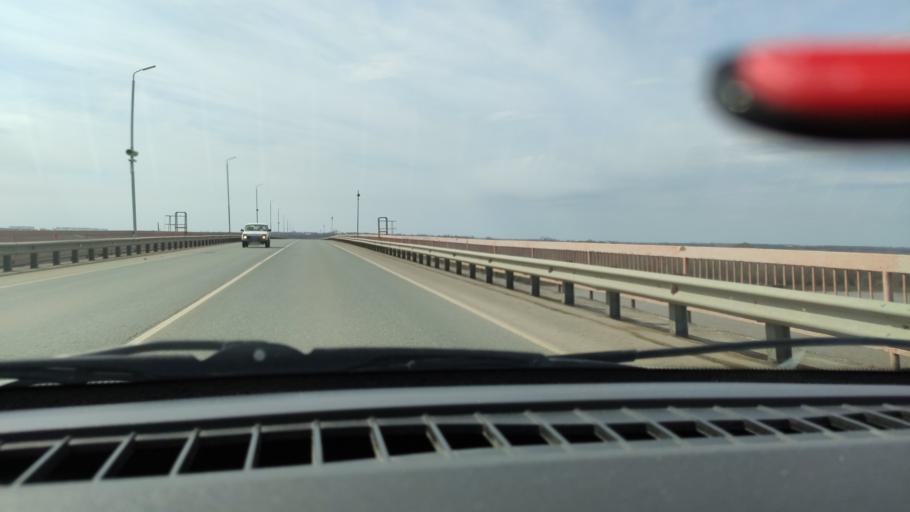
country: RU
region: Bashkortostan
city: Dyurtyuli
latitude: 55.5284
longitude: 54.8467
